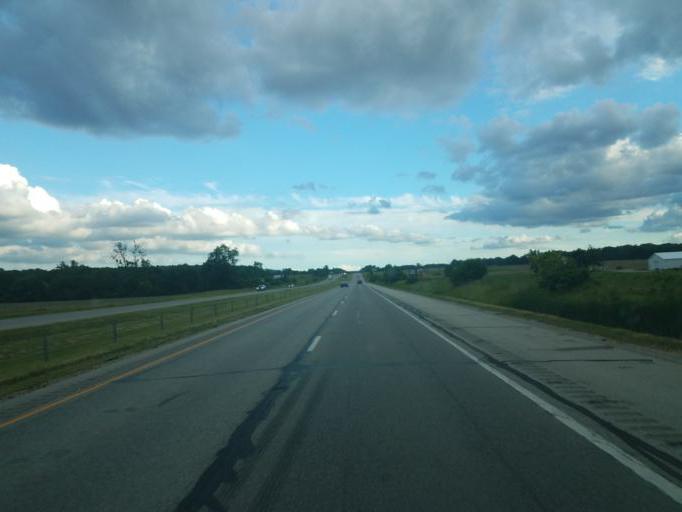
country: US
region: Indiana
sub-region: DeKalb County
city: Garrett
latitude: 41.2908
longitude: -85.0873
